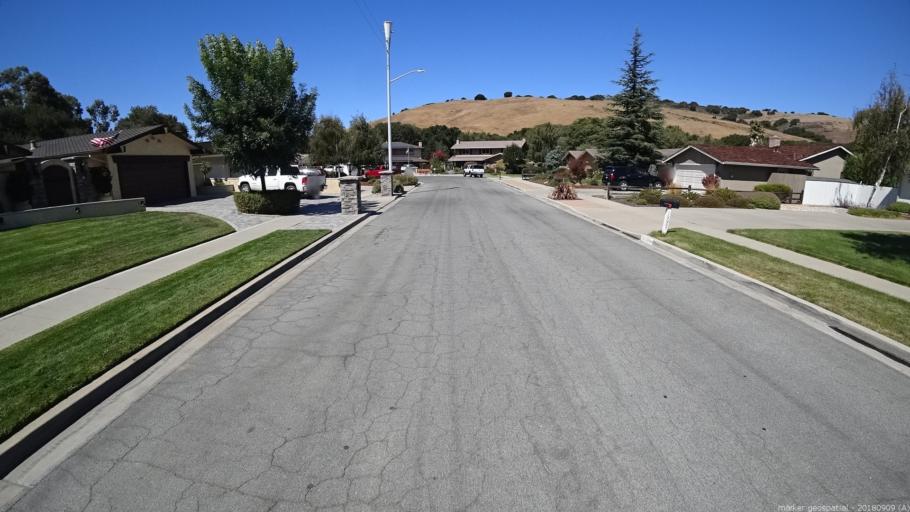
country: US
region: California
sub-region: Monterey County
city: Salinas
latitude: 36.6155
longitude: -121.6893
